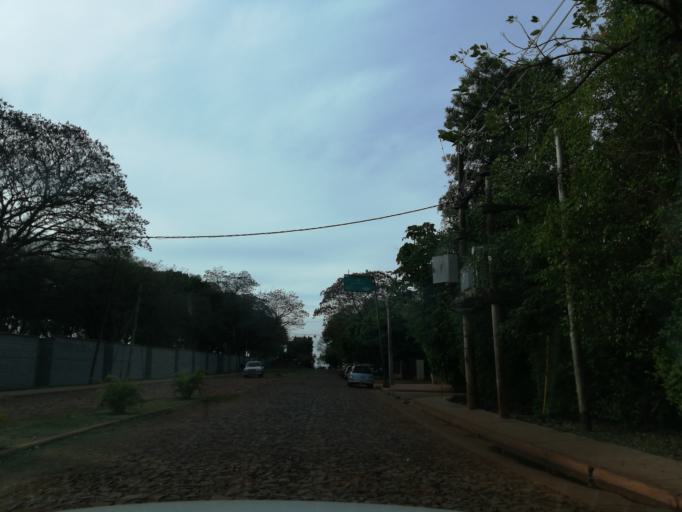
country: AR
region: Misiones
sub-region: Departamento de Capital
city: Posadas
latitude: -27.3556
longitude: -55.9263
